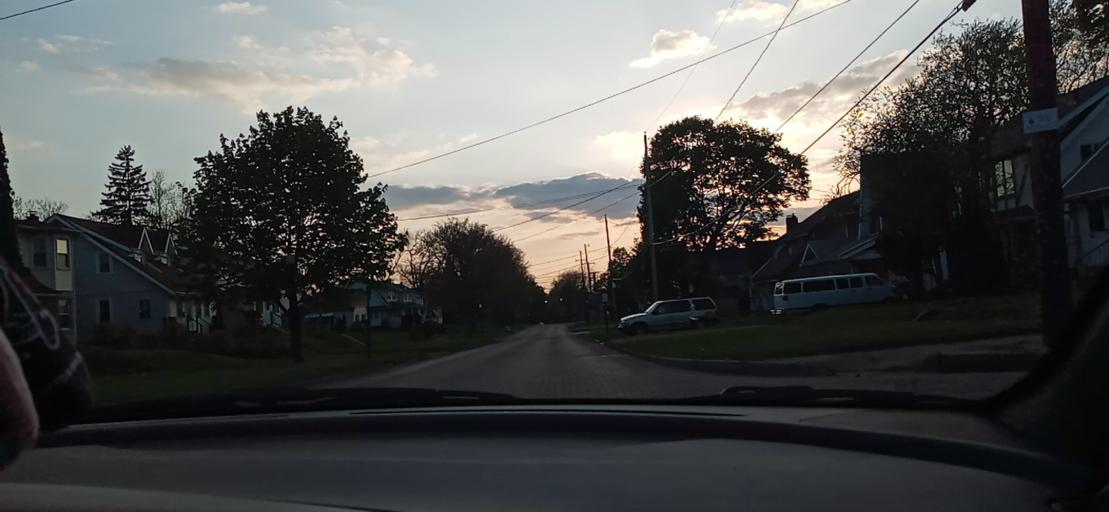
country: US
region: Ohio
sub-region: Summit County
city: Akron
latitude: 41.0446
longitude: -81.5081
